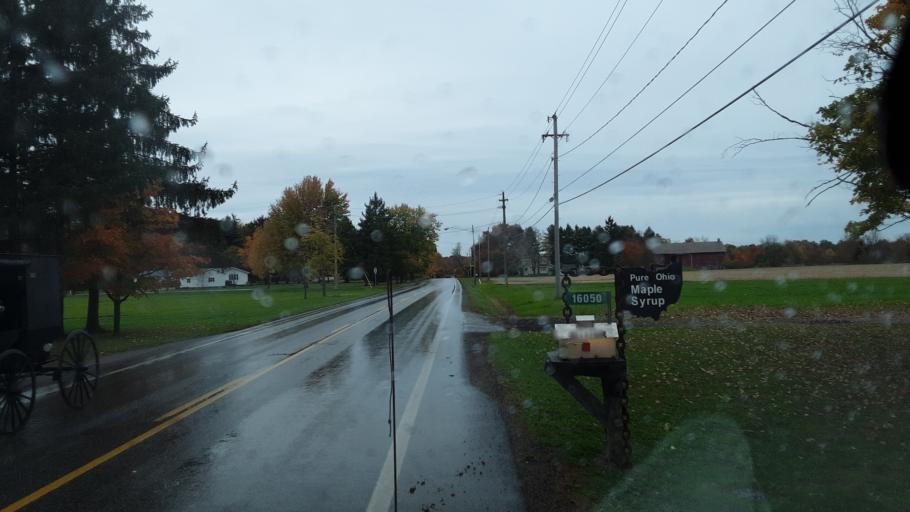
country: US
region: Ohio
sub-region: Geauga County
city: Middlefield
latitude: 41.4326
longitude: -81.1096
